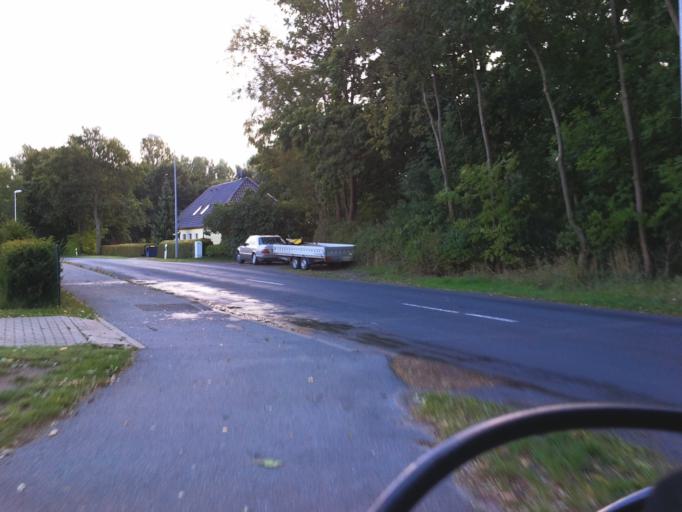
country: DE
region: Mecklenburg-Vorpommern
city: Dierkow-West
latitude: 54.1248
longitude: 12.1054
